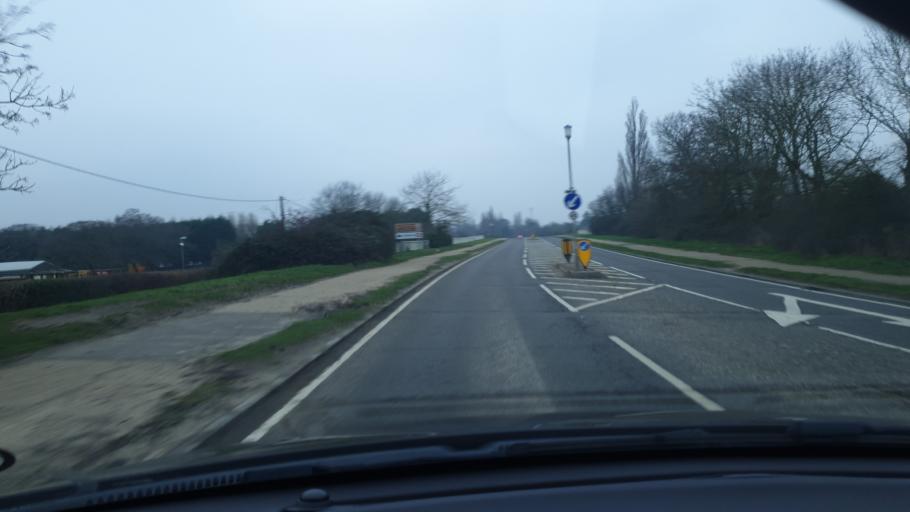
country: GB
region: England
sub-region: Essex
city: Little Clacton
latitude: 51.8515
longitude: 1.1169
